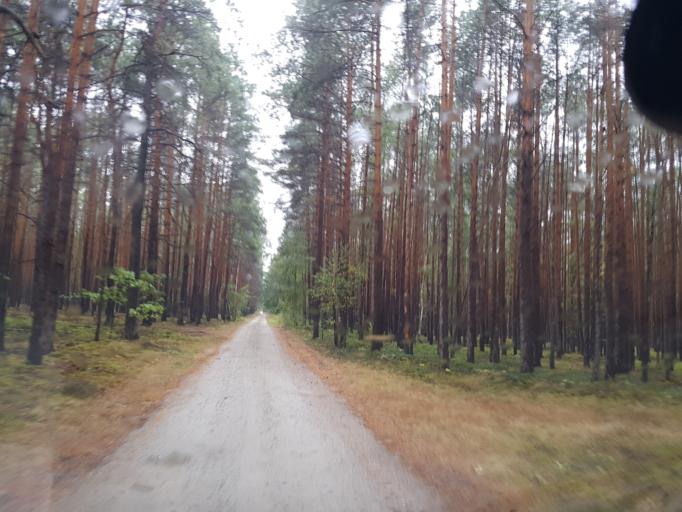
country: DE
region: Brandenburg
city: Sallgast
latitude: 51.6114
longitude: 13.7787
